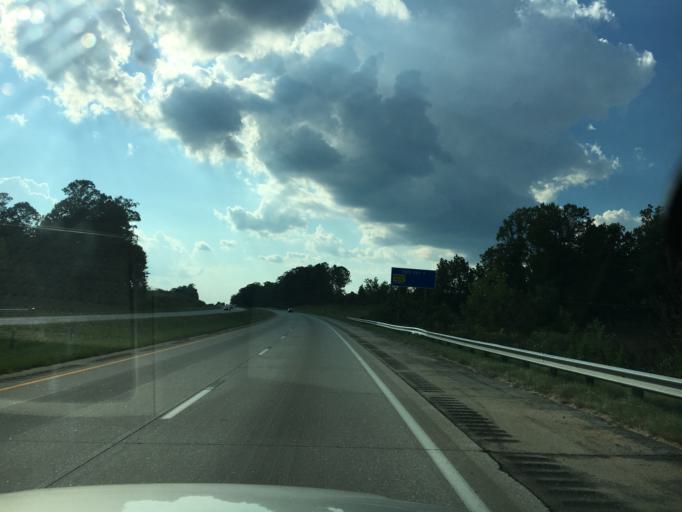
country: US
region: South Carolina
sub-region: Laurens County
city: Watts Mills
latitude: 34.5503
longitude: -81.9890
